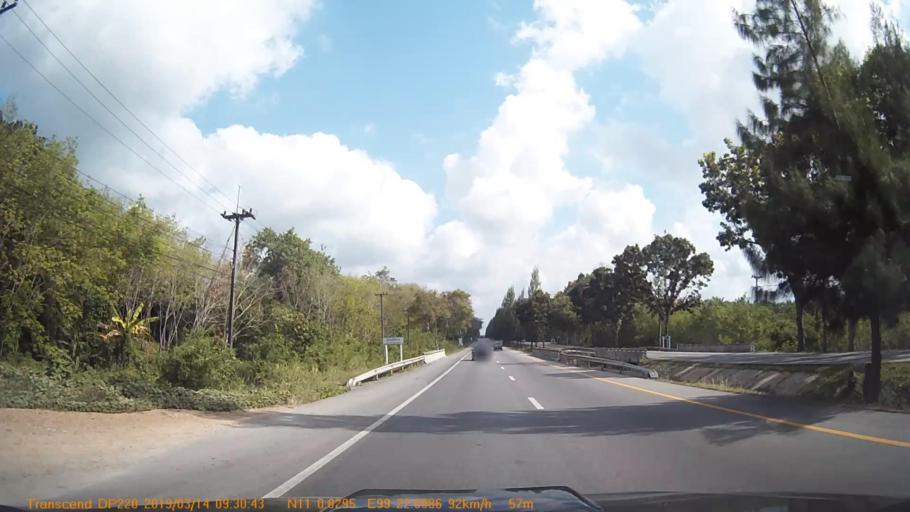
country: TH
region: Prachuap Khiri Khan
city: Bang Saphan Noi
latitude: 11.0148
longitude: 99.3685
